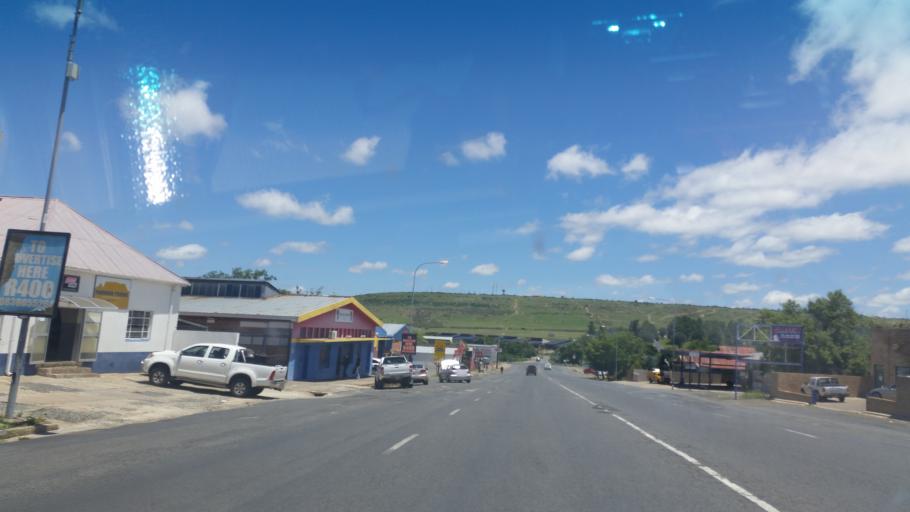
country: ZA
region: Orange Free State
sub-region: Thabo Mofutsanyana District Municipality
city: Harrismith
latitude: -28.2654
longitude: 29.1204
